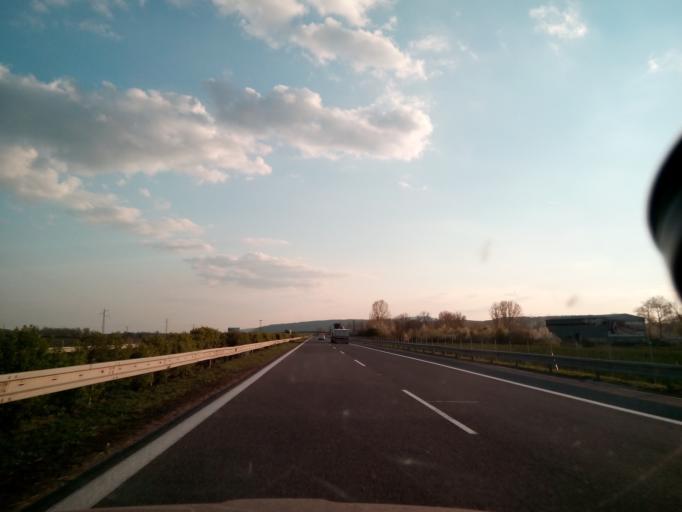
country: SK
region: Trenciansky
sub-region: Okres Nove Mesto nad Vahom
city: Nove Mesto nad Vahom
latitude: 48.8295
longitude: 17.9234
